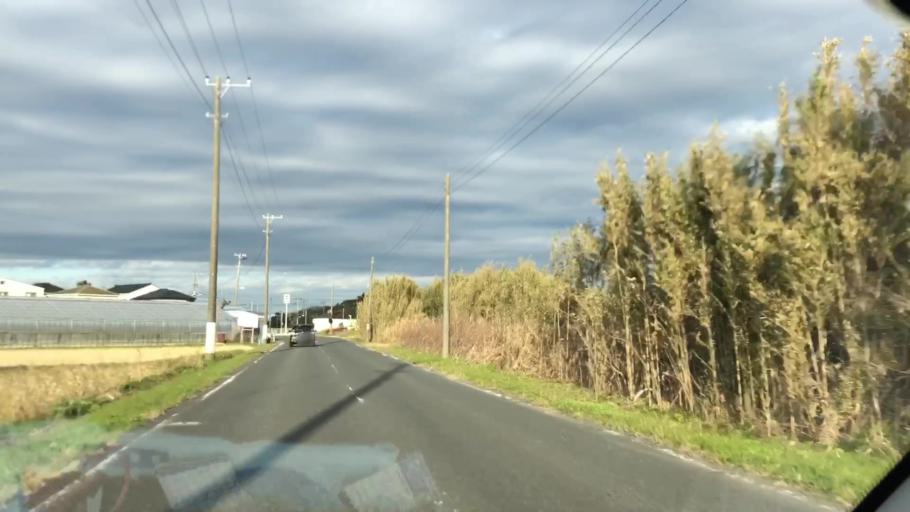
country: JP
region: Chiba
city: Tateyama
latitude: 35.0055
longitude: 139.8824
